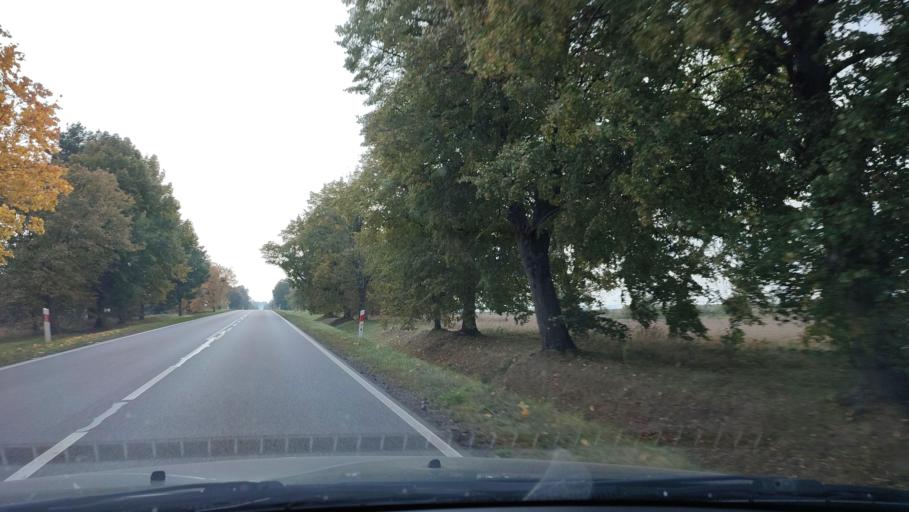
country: PL
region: Warmian-Masurian Voivodeship
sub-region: Powiat nidzicki
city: Kozlowo
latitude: 53.3409
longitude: 20.3405
